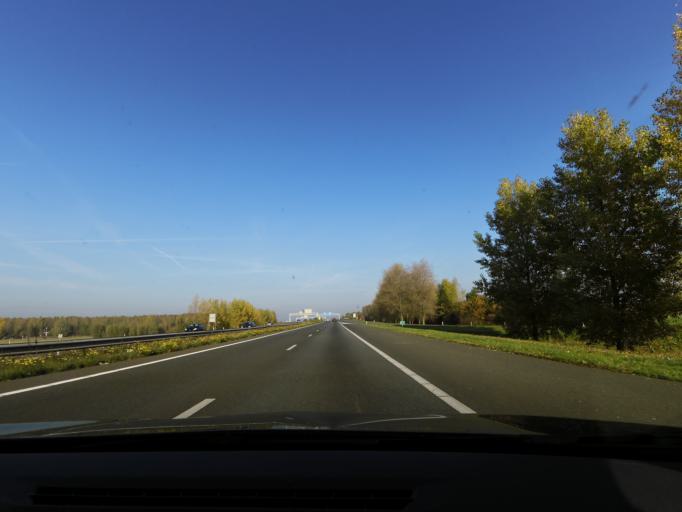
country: NL
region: South Holland
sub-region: Gemeente Strijen
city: Strijen
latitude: 51.6911
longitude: 4.6391
